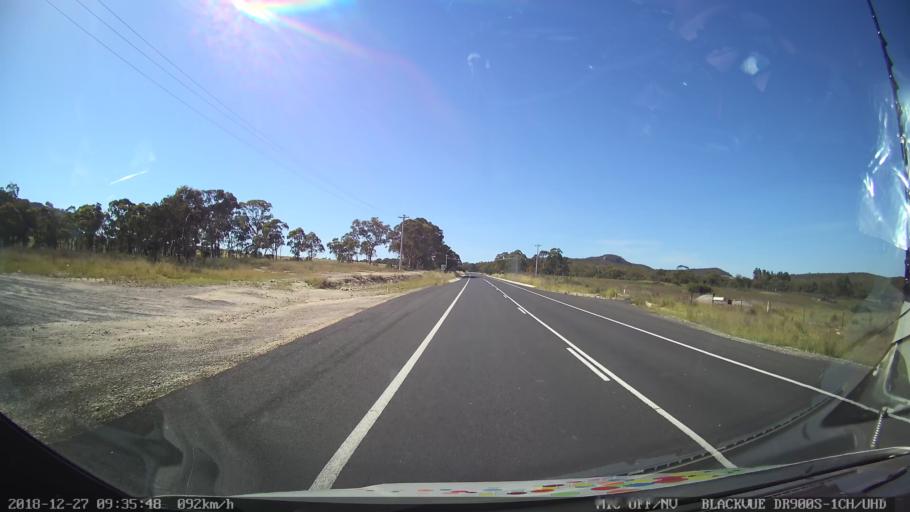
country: AU
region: New South Wales
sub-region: Lithgow
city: Portland
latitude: -33.2434
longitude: 150.0323
